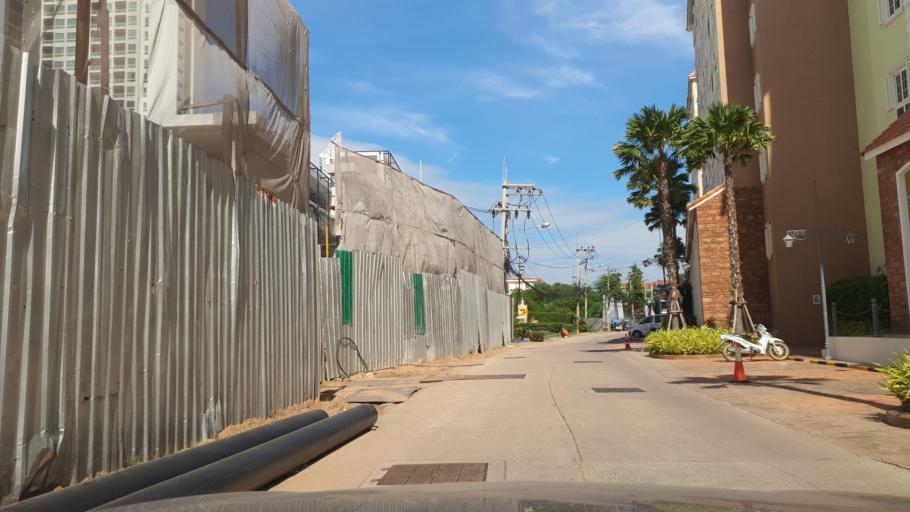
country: TH
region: Chon Buri
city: Phatthaya
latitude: 12.8593
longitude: 100.8999
